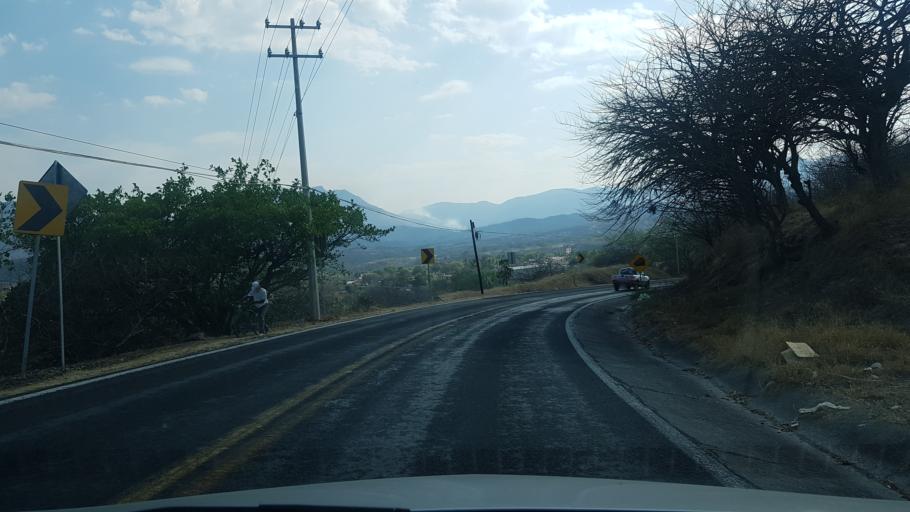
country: MX
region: Morelos
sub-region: Amacuzac
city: Amacuzac
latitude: 18.6032
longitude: -99.3650
